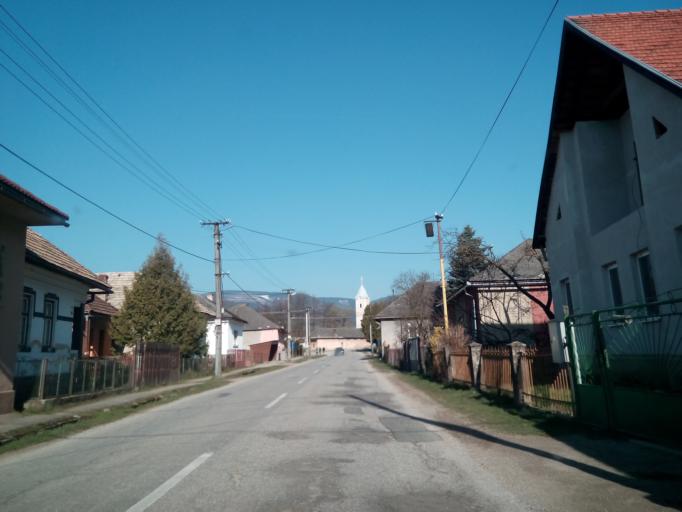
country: SK
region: Kosicky
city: Dobsina
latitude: 48.7017
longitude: 20.3021
